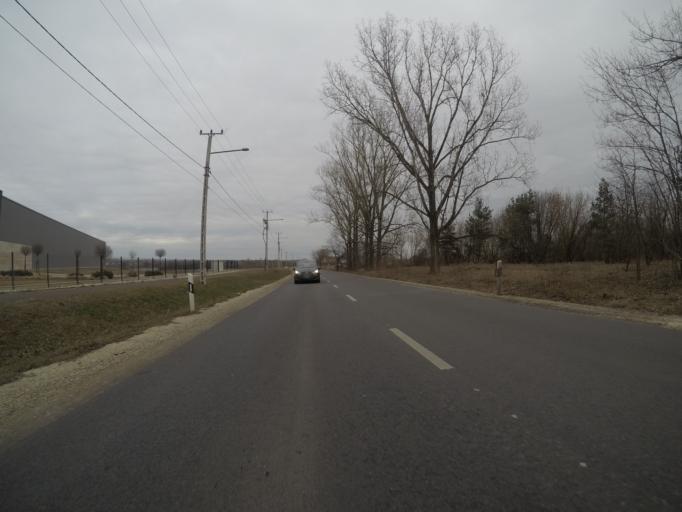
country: HU
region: Pest
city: Tapioszecso
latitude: 47.4479
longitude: 19.5809
